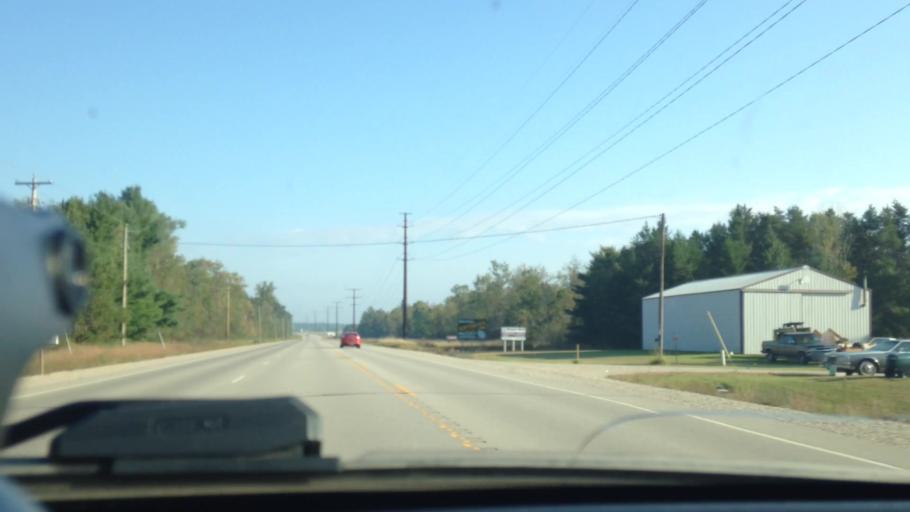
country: US
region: Wisconsin
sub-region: Marinette County
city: Peshtigo
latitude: 45.1888
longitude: -87.9952
